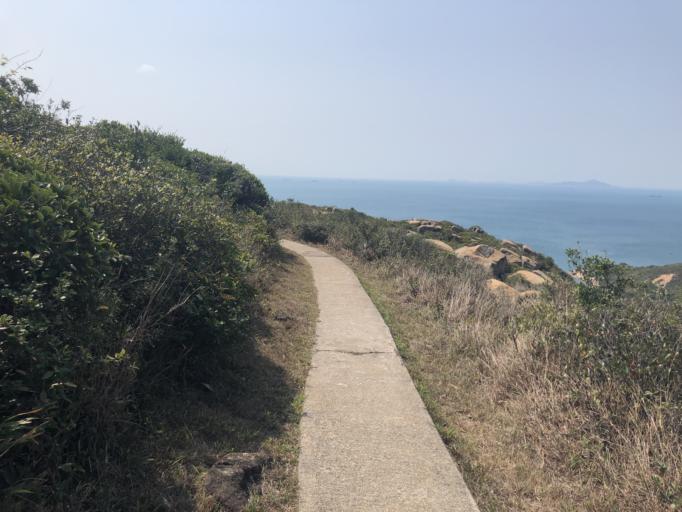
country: HK
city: Sok Kwu Wan
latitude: 22.1669
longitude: 114.2607
